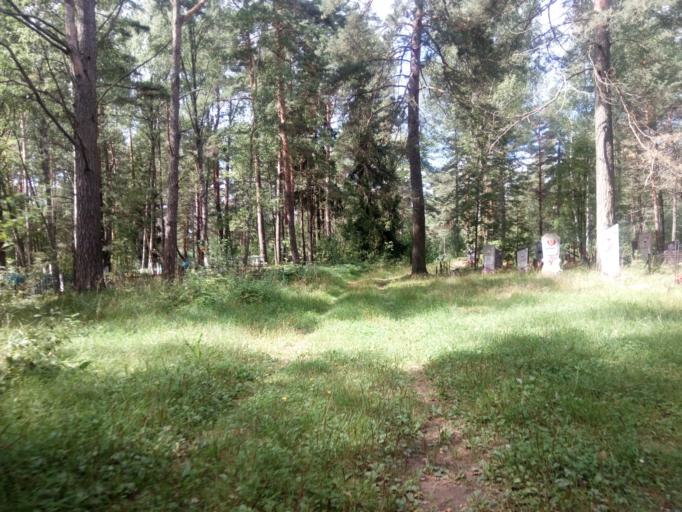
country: BY
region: Vitebsk
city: Dzisna
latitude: 55.6803
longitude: 28.2819
